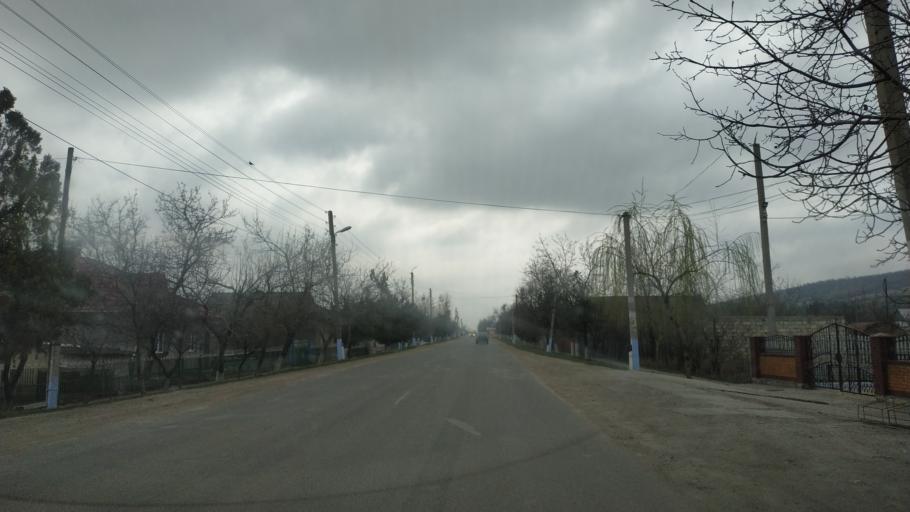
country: MD
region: Basarabeasca
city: Basarabeasca
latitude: 46.3616
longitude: 28.9358
